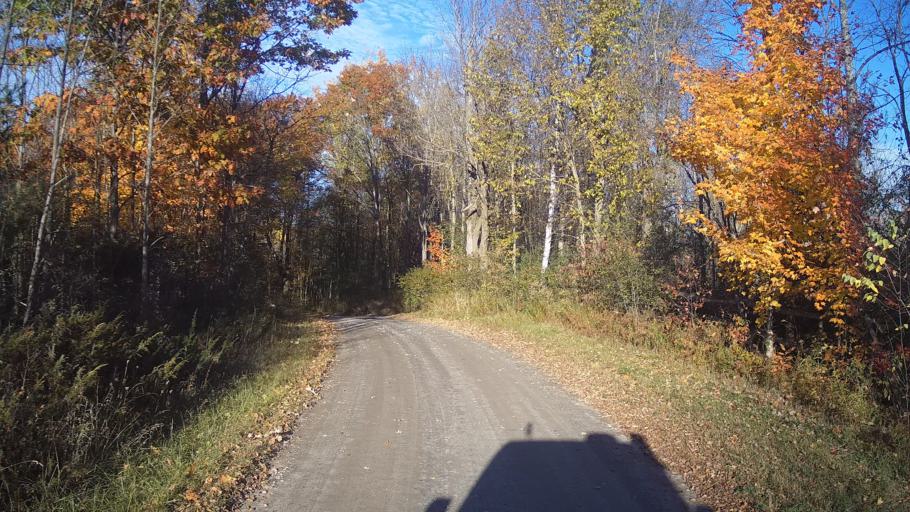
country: CA
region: Ontario
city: Perth
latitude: 44.7386
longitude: -76.4129
